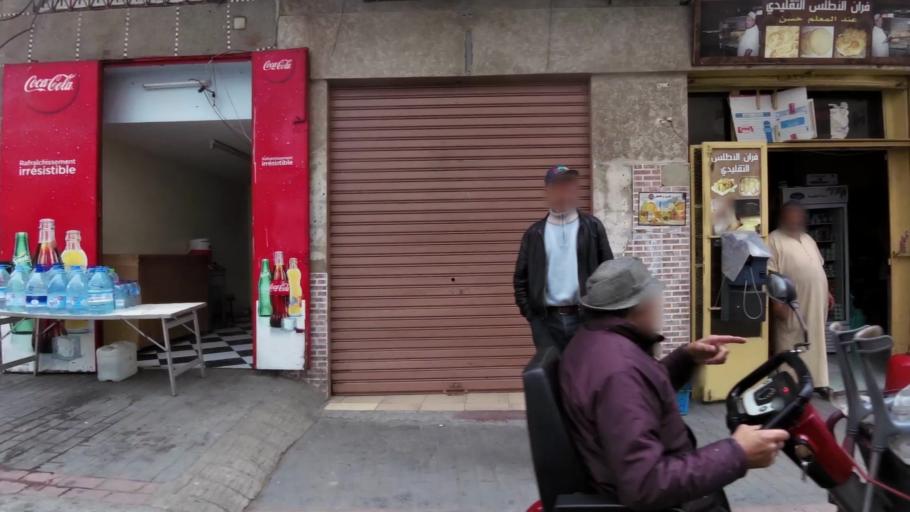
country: MA
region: Tanger-Tetouan
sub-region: Tanger-Assilah
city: Tangier
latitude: 35.7677
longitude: -5.8208
